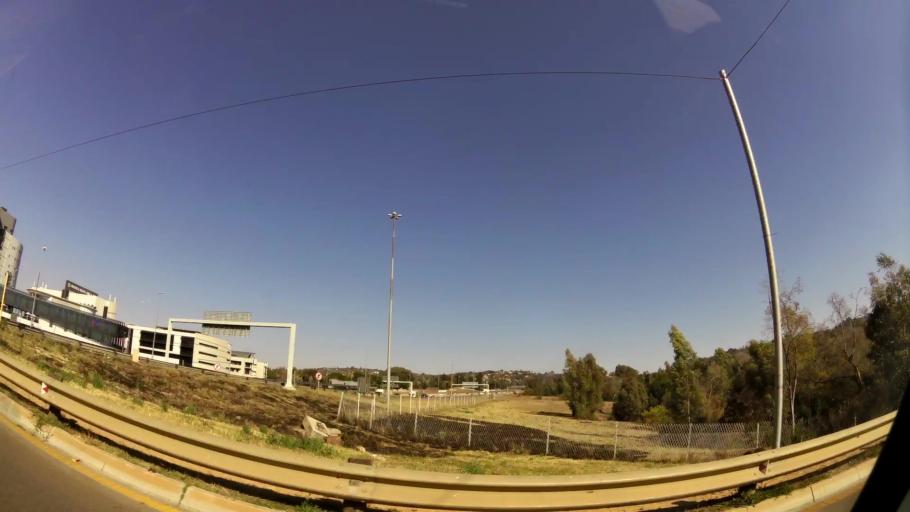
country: ZA
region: Gauteng
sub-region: City of Tshwane Metropolitan Municipality
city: Pretoria
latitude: -25.7850
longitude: 28.2693
